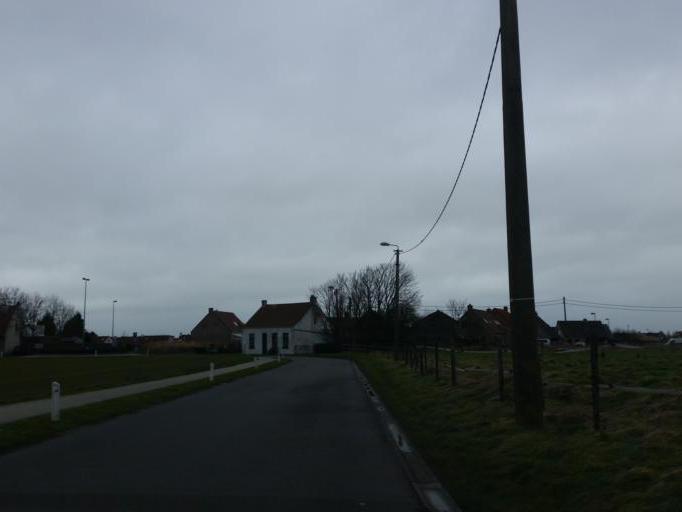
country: BE
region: Flanders
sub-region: Provincie West-Vlaanderen
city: Bredene
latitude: 51.2447
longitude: 2.9879
